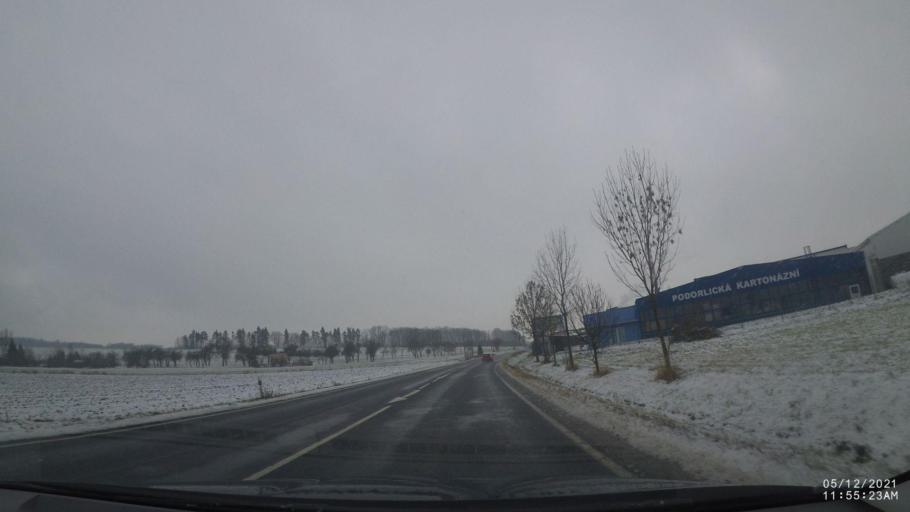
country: CZ
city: Dobruska
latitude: 50.2869
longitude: 16.1660
